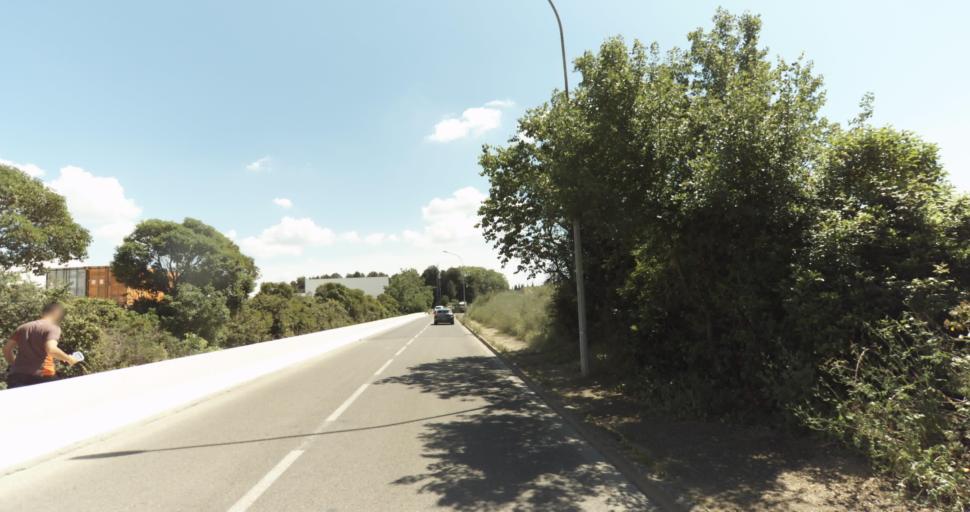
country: FR
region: Languedoc-Roussillon
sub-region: Departement du Gard
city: Milhaud
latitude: 43.8073
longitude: 4.3286
